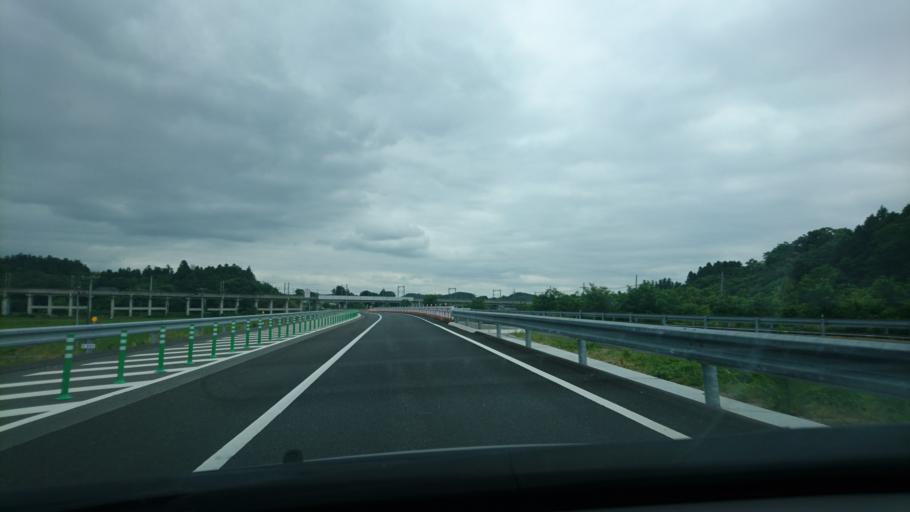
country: JP
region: Miyagi
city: Kogota
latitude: 38.7311
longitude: 141.0566
